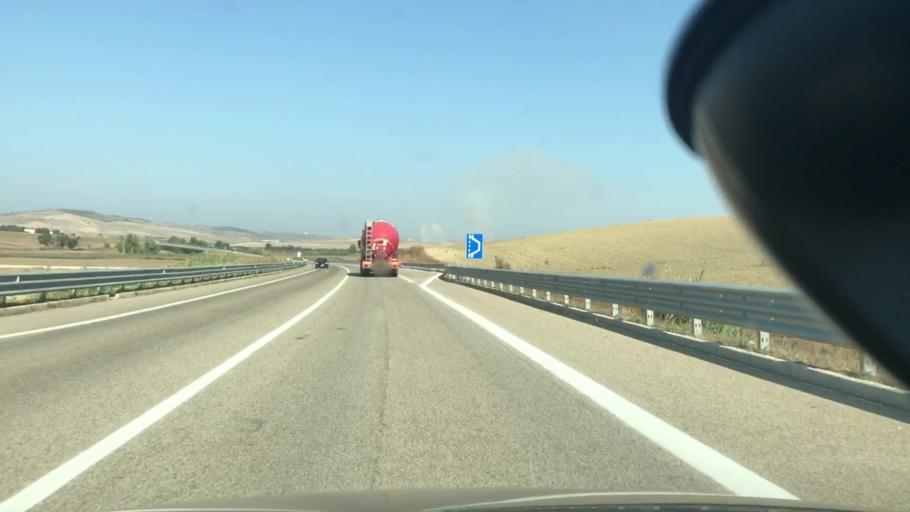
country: IT
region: Basilicate
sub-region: Provincia di Matera
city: Irsina
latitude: 40.7788
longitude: 16.3173
